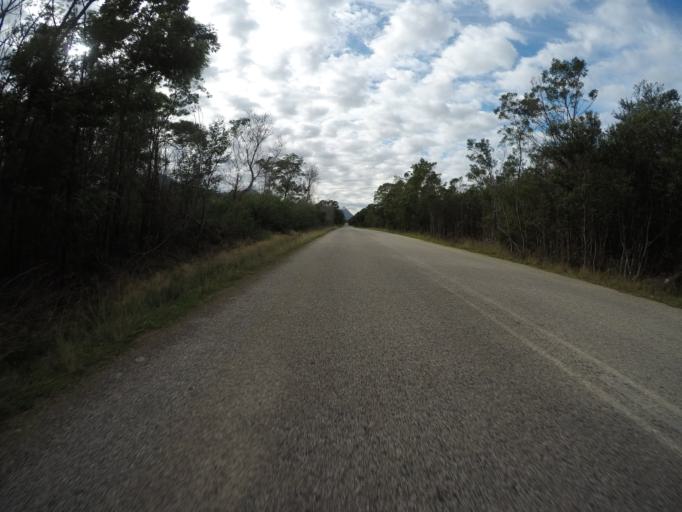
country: ZA
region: Eastern Cape
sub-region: Cacadu District Municipality
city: Kareedouw
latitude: -34.0163
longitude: 24.3345
